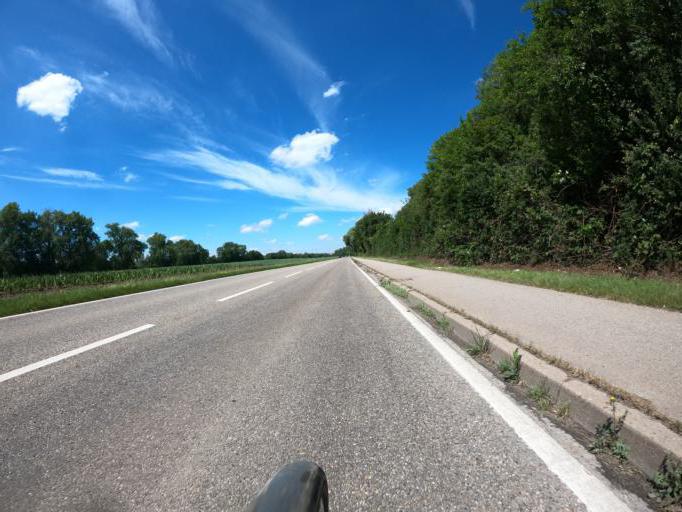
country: DE
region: Baden-Wuerttemberg
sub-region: Regierungsbezirk Stuttgart
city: Asperg
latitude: 48.9060
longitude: 9.1224
